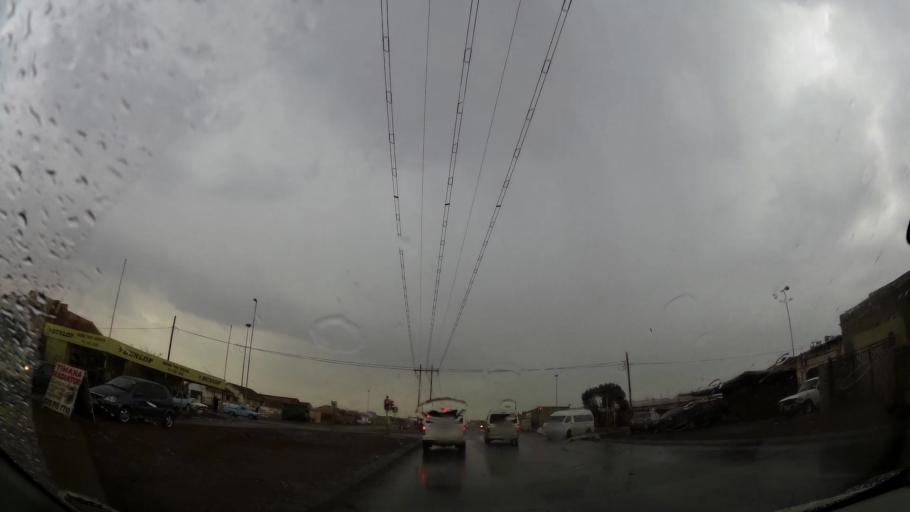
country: ZA
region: Gauteng
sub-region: Ekurhuleni Metropolitan Municipality
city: Germiston
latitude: -26.3589
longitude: 28.1502
